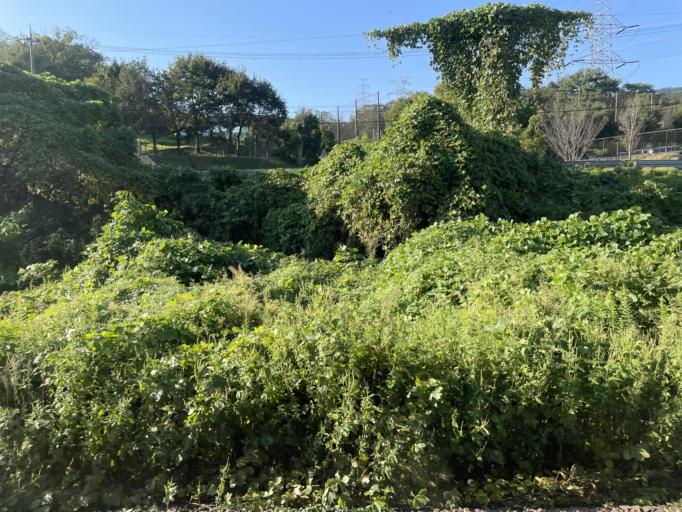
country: JP
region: Osaka
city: Kashihara
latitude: 34.5532
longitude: 135.6593
